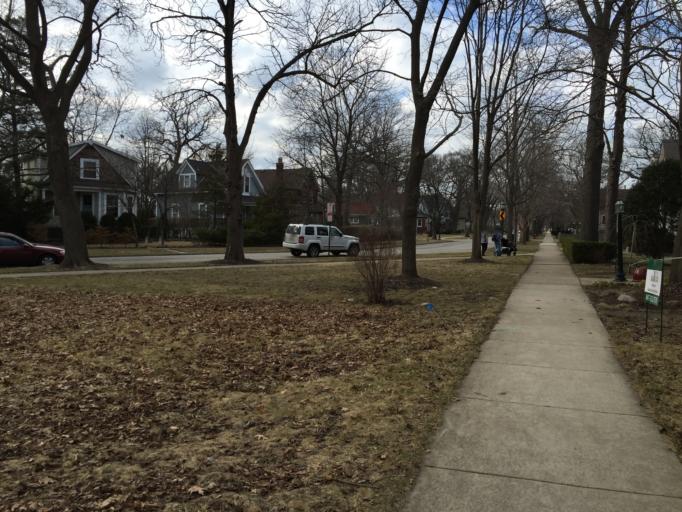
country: US
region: Illinois
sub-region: Cook County
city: Wilmette
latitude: 42.0721
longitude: -87.7077
